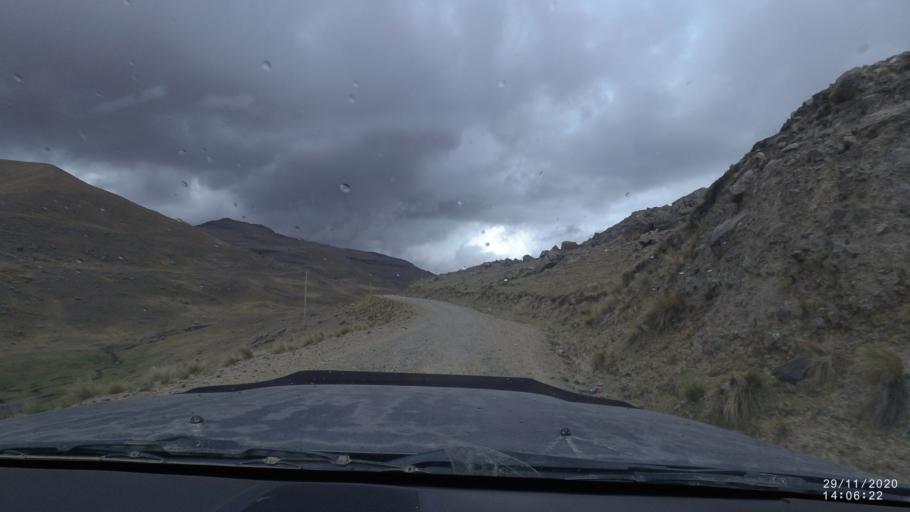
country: BO
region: Cochabamba
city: Sipe Sipe
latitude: -17.2133
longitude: -66.3782
